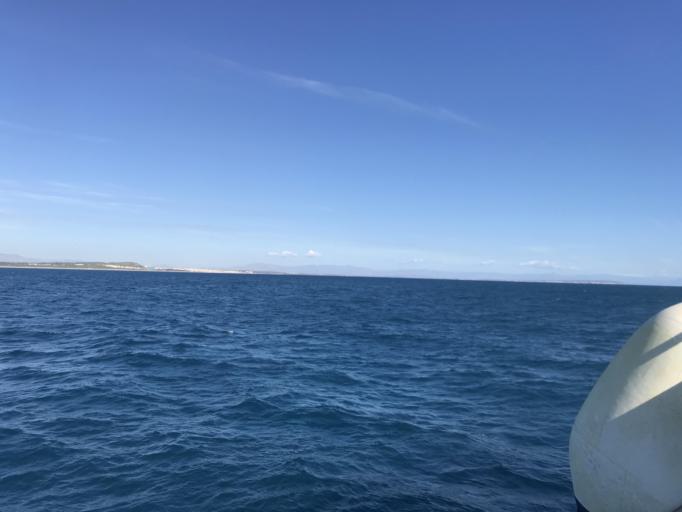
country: ES
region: Valencia
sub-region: Provincia de Alicante
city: Torrevieja
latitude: 38.0130
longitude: -0.6273
